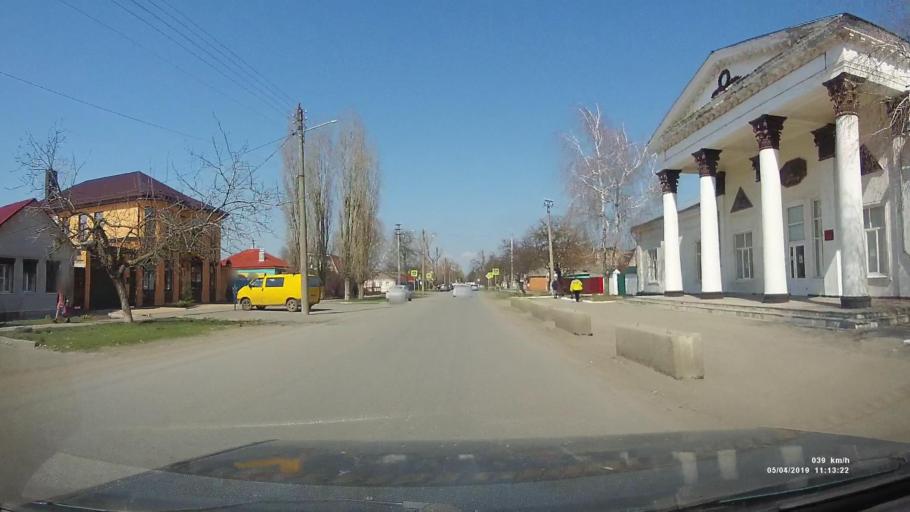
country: RU
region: Rostov
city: Azov
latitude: 47.1019
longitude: 39.4317
